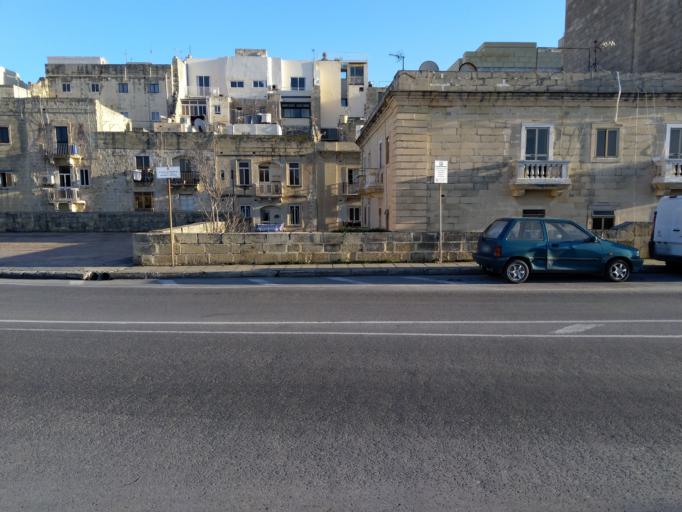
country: MT
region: Il-Belt Valletta
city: Valletta
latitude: 35.9018
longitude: 14.5166
